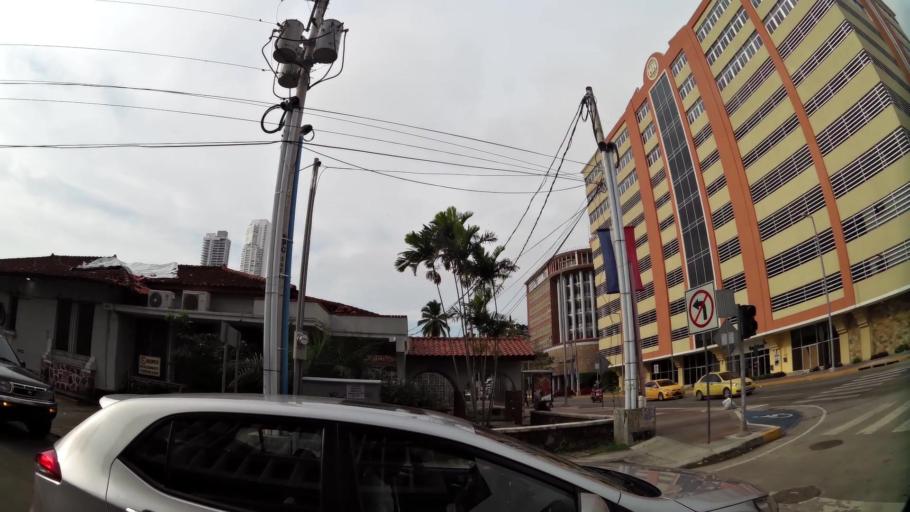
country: PA
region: Panama
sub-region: Distrito de Panama
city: Ancon
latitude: 8.9726
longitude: -79.5327
